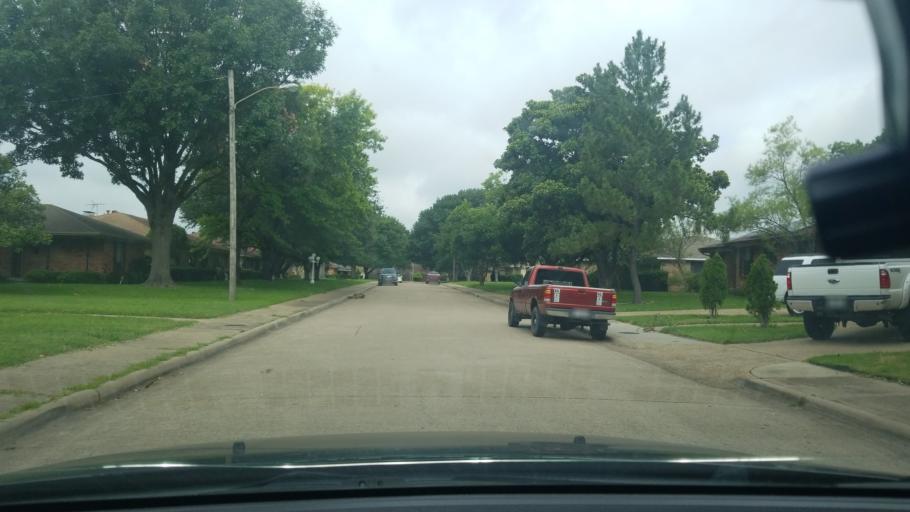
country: US
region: Texas
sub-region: Dallas County
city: Balch Springs
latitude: 32.7905
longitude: -96.6916
